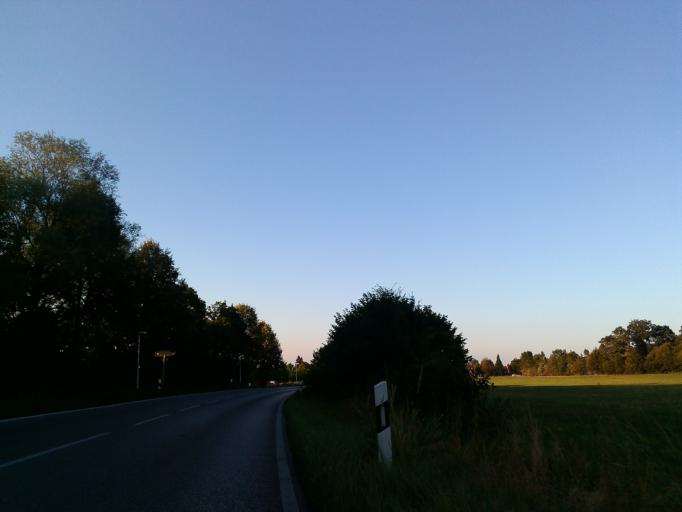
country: DE
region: Bavaria
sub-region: Upper Bavaria
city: Krailling
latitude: 48.0793
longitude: 11.3969
